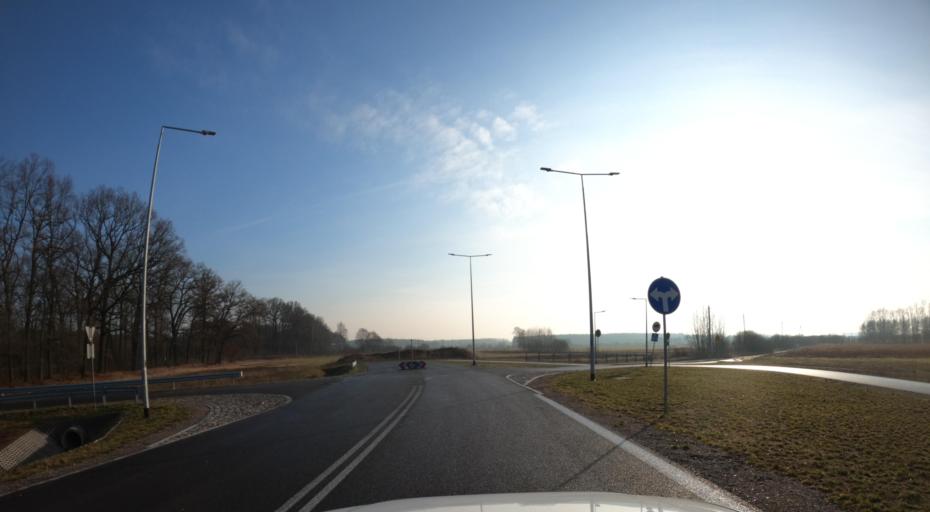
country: PL
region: Lubusz
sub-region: Powiat gorzowski
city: Kostrzyn nad Odra
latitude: 52.6229
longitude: 14.6257
